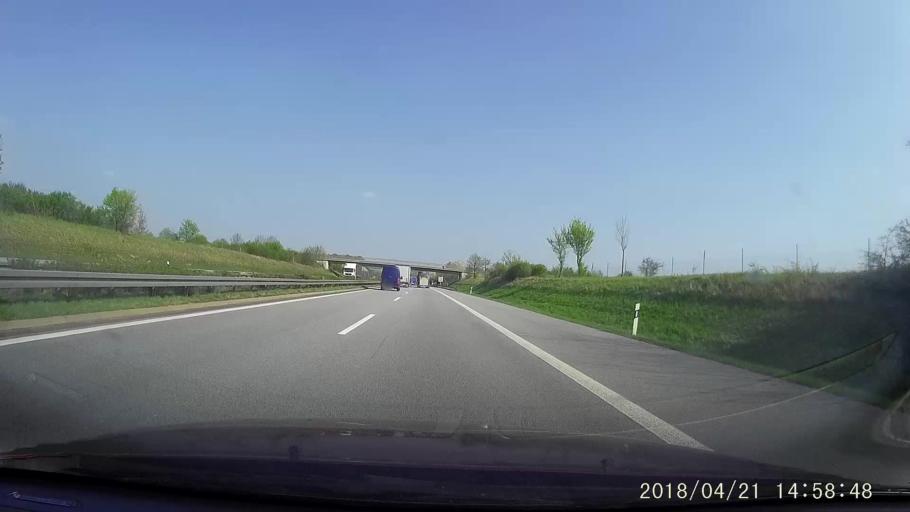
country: DE
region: Saxony
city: Quitzdorf
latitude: 51.2056
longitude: 14.7439
